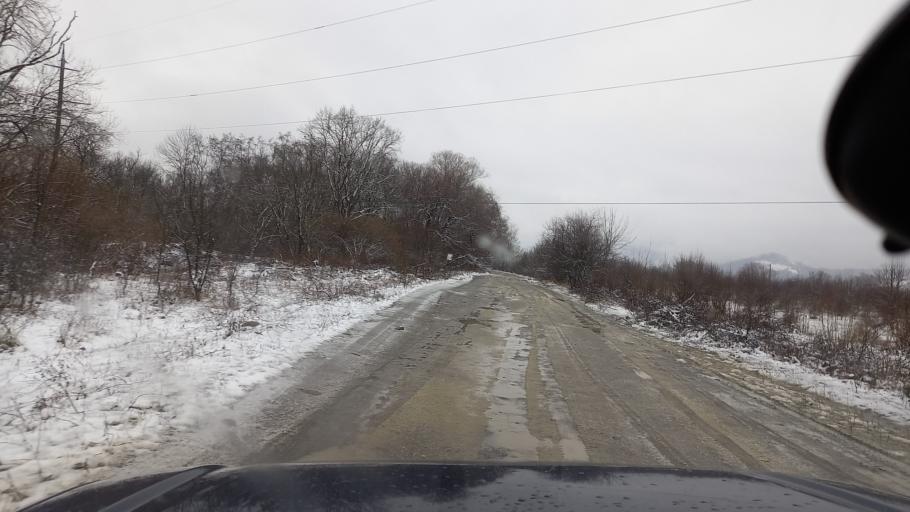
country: RU
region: Adygeya
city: Kamennomostskiy
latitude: 44.2291
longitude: 40.1862
